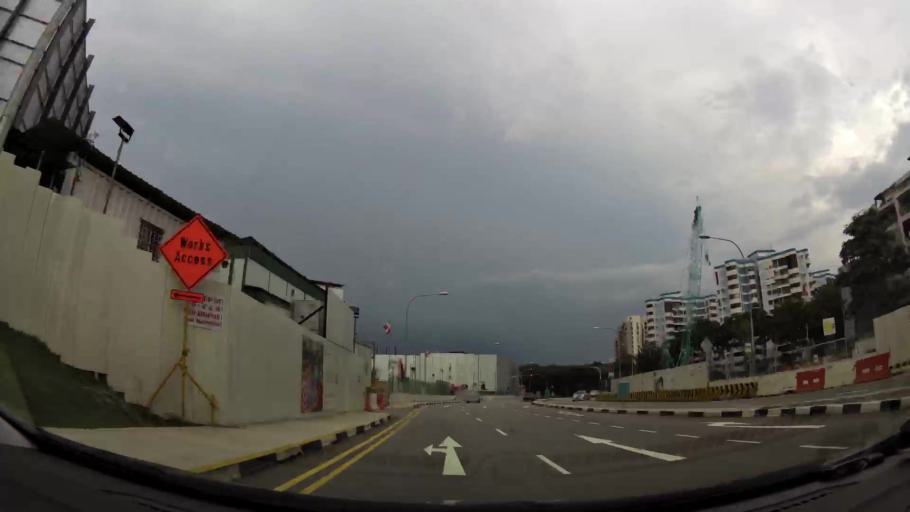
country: SG
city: Singapore
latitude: 1.3836
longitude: 103.8366
